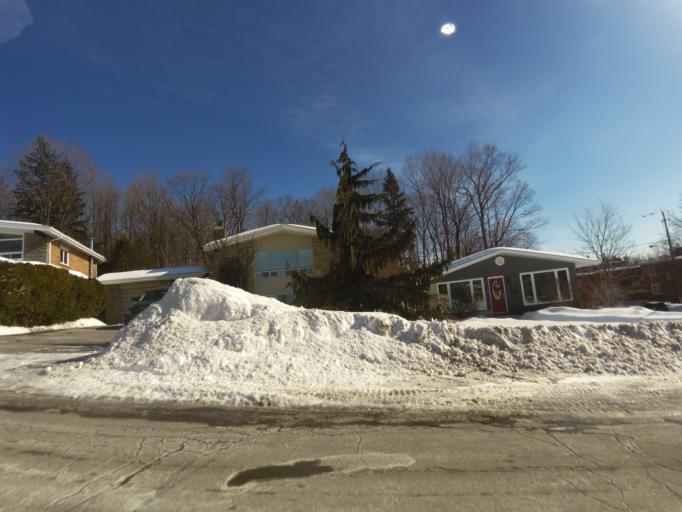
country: CA
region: Ontario
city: Ottawa
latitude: 45.4438
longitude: -75.6648
